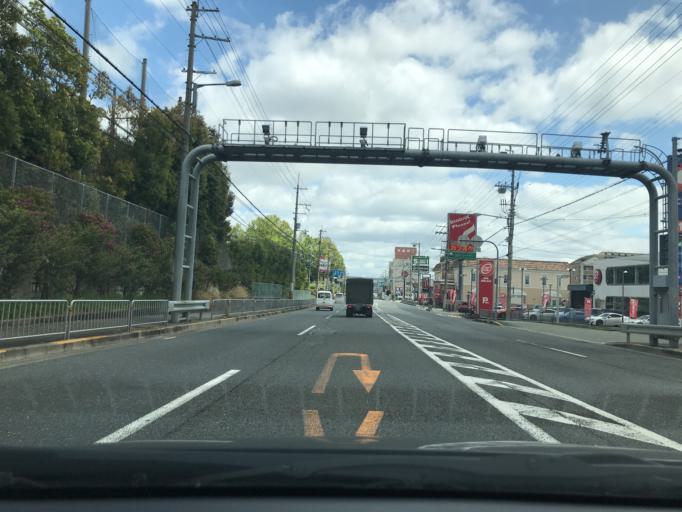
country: JP
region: Osaka
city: Mino
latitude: 34.8360
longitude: 135.5208
